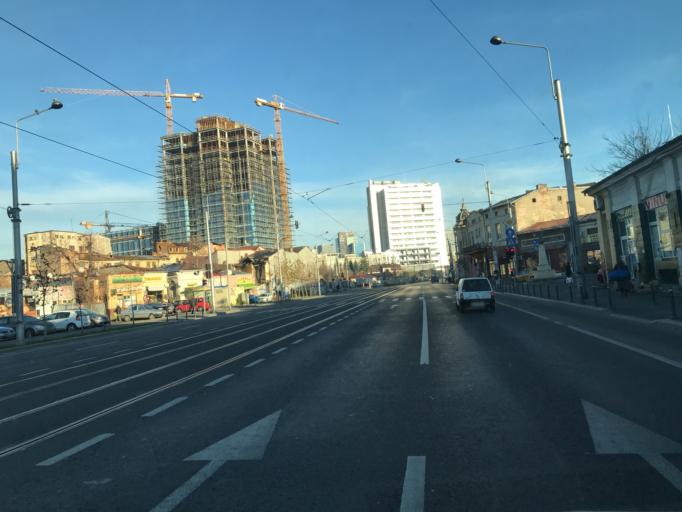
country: RO
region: Bucuresti
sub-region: Municipiul Bucuresti
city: Bucuresti
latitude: 44.4445
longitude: 26.0813
